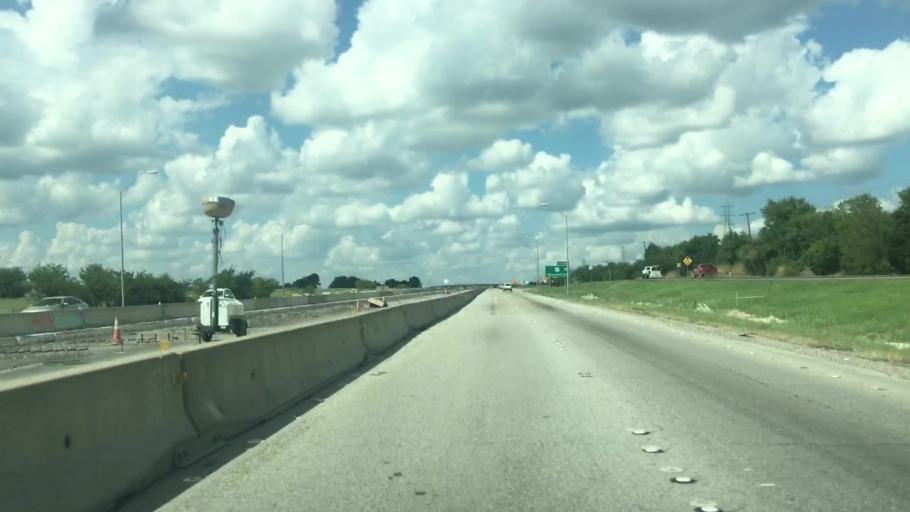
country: US
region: Texas
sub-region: Ellis County
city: Waxahachie
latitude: 32.3505
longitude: -96.8545
